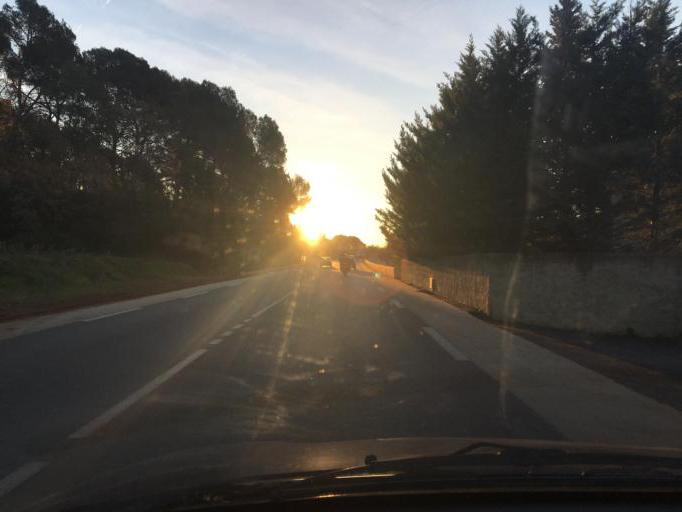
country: FR
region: Provence-Alpes-Cote d'Azur
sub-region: Departement du Var
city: Taradeau
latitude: 43.4635
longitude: 6.4004
